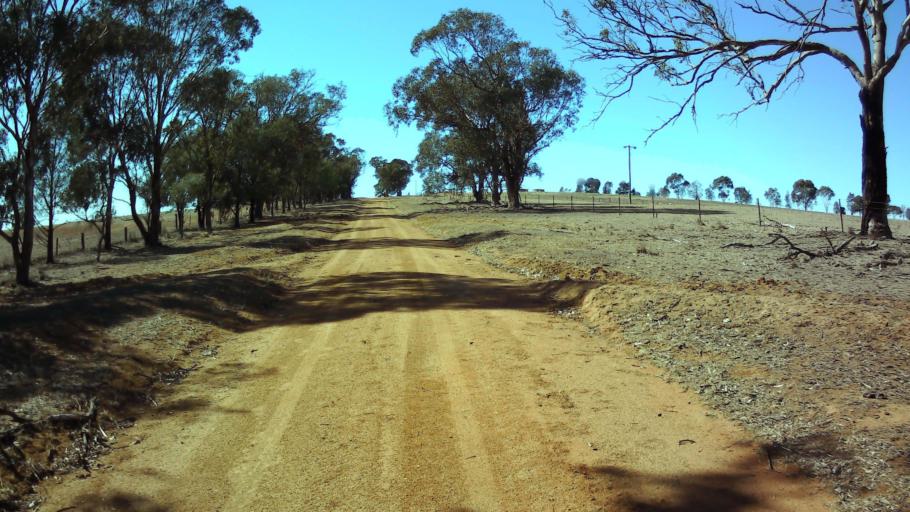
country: AU
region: New South Wales
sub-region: Cowra
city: Cowra
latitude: -33.9725
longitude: 148.4612
